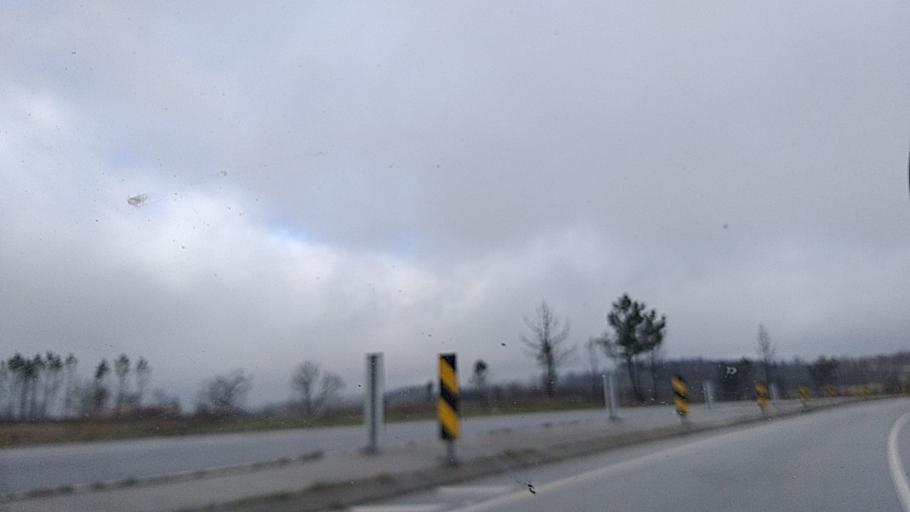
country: PT
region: Guarda
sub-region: Fornos de Algodres
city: Fornos de Algodres
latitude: 40.6932
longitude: -7.4729
